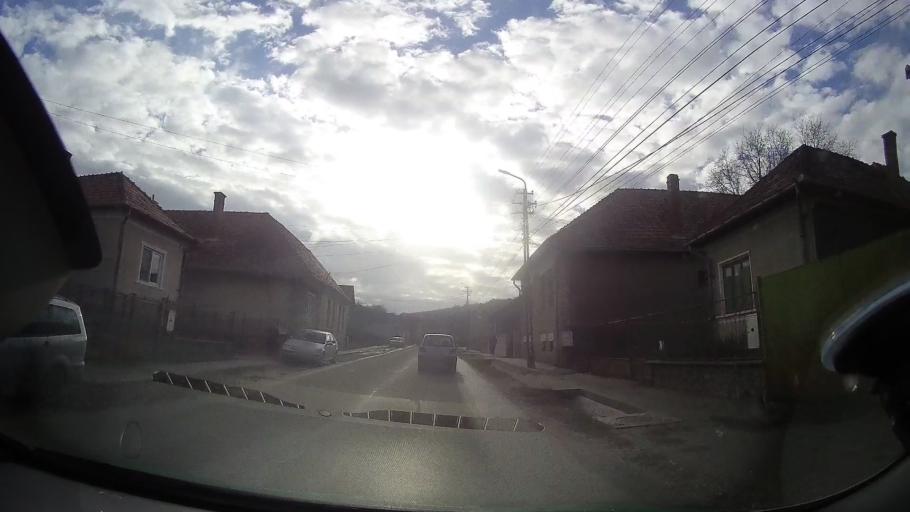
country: RO
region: Cluj
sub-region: Comuna Savadisla
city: Savadisla
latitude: 46.6766
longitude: 23.4565
